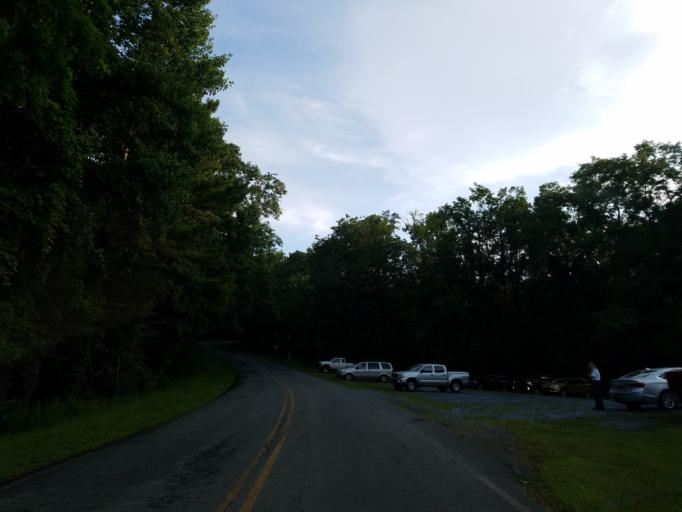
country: US
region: Georgia
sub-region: Pickens County
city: Jasper
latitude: 34.5434
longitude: -84.4370
